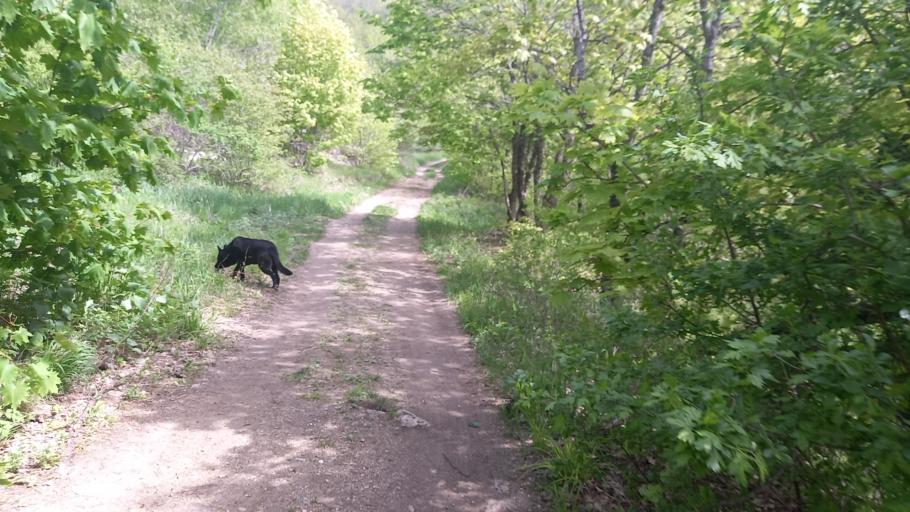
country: RU
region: Stavropol'skiy
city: Pyatigorsk
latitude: 44.0891
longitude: 43.0296
